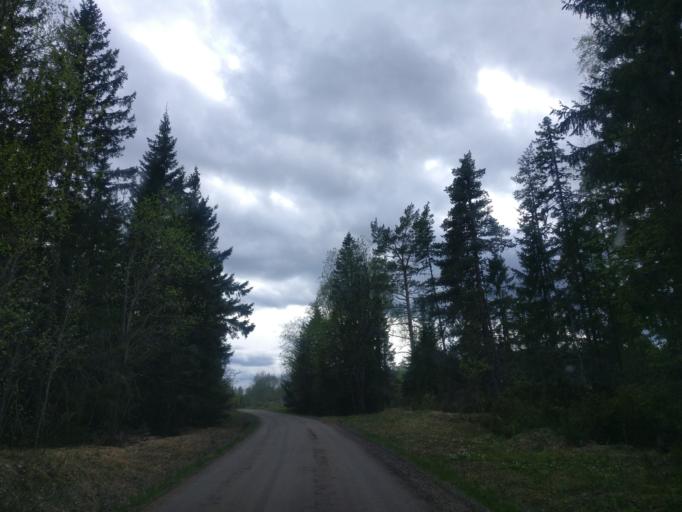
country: SE
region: Vaesternorrland
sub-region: Timra Kommun
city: Soraker
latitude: 62.5157
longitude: 17.5561
